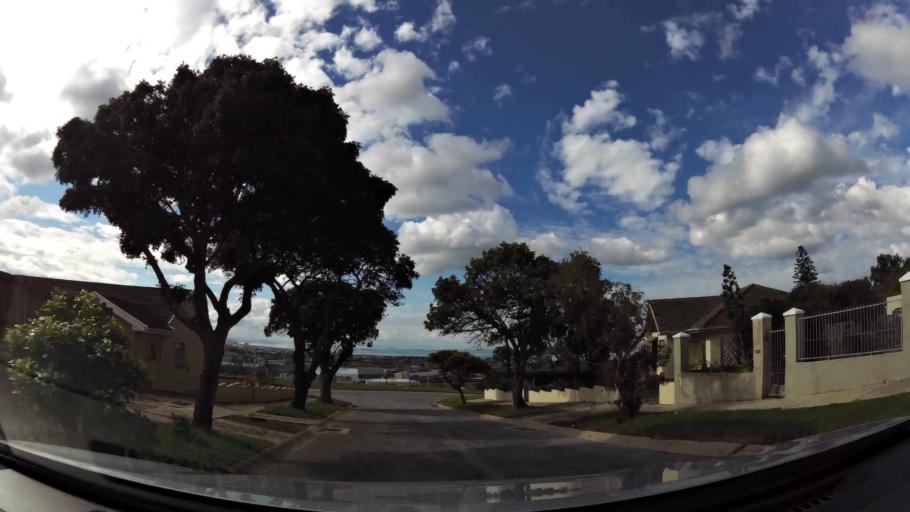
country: ZA
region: Eastern Cape
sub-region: Nelson Mandela Bay Metropolitan Municipality
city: Port Elizabeth
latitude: -33.9416
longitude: 25.5843
